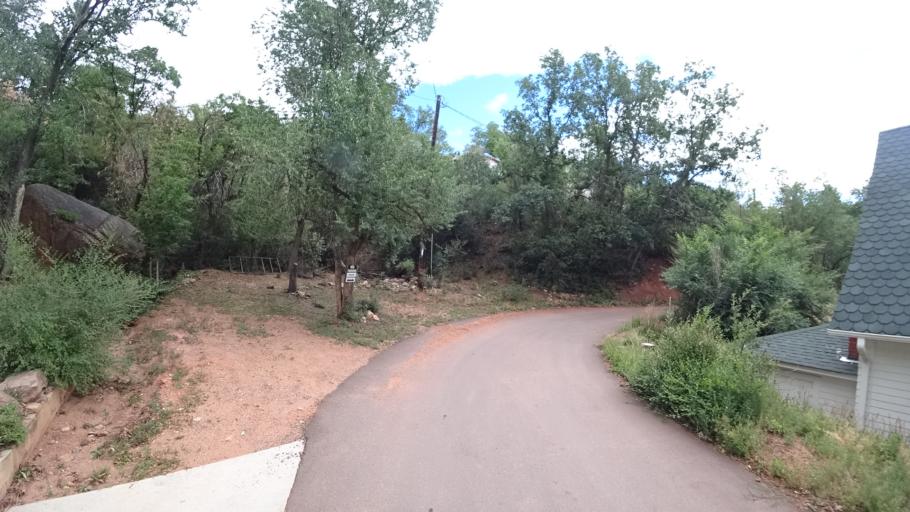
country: US
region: Colorado
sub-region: El Paso County
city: Manitou Springs
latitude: 38.8593
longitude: -104.9237
